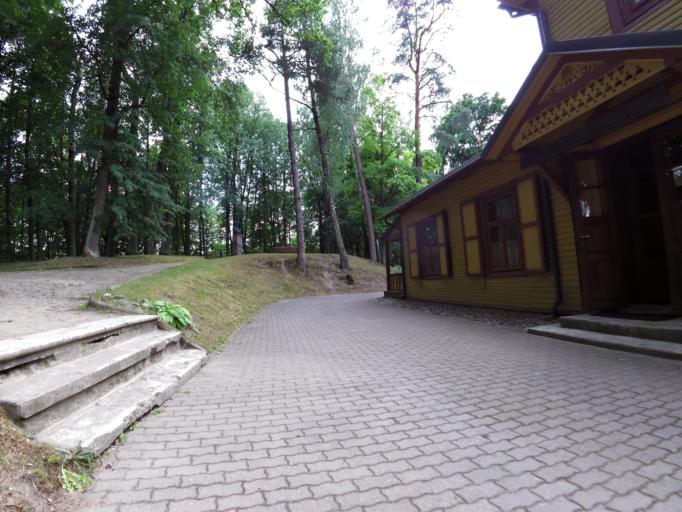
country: LT
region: Vilnius County
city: Rasos
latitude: 54.6740
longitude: 25.3256
